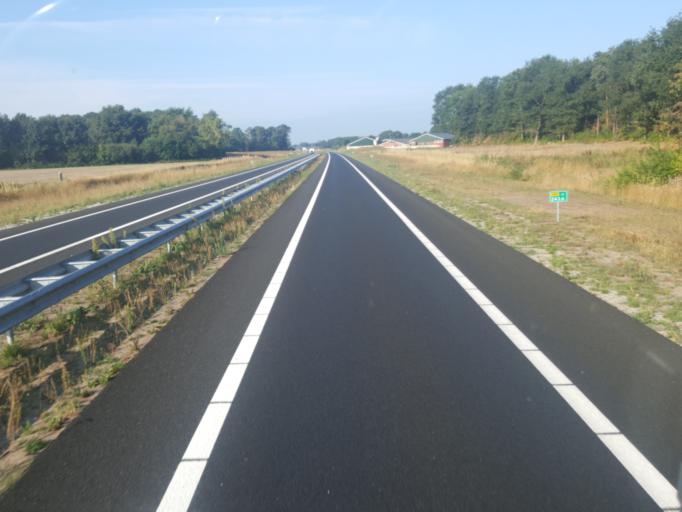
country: NL
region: Gelderland
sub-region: Berkelland
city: Eibergen
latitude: 52.1256
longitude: 6.6513
